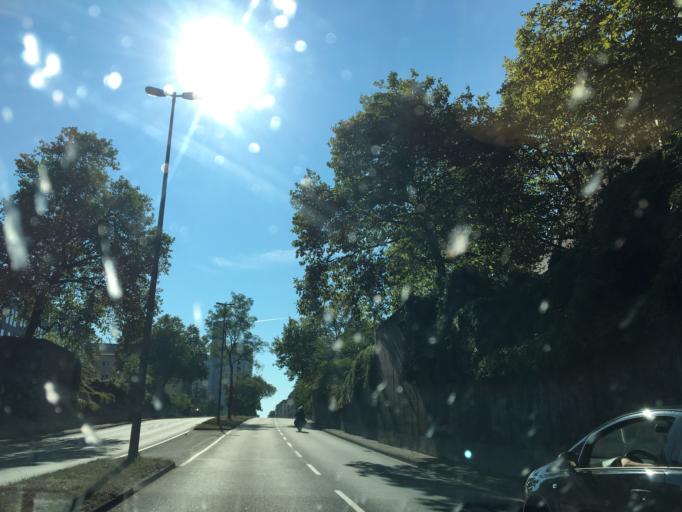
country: DE
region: North Rhine-Westphalia
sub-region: Regierungsbezirk Koln
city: Neustadt/Sued
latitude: 50.9281
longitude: 6.9283
